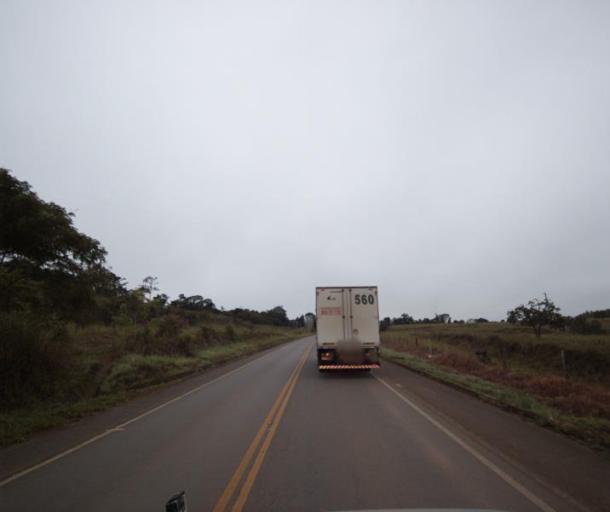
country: BR
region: Goias
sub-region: Pirenopolis
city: Pirenopolis
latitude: -15.9587
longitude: -48.8141
